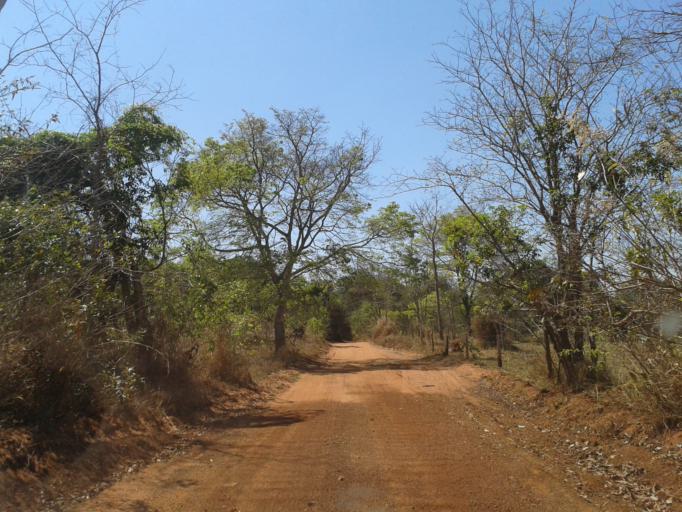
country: BR
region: Minas Gerais
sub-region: Ituiutaba
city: Ituiutaba
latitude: -19.0956
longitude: -49.2973
